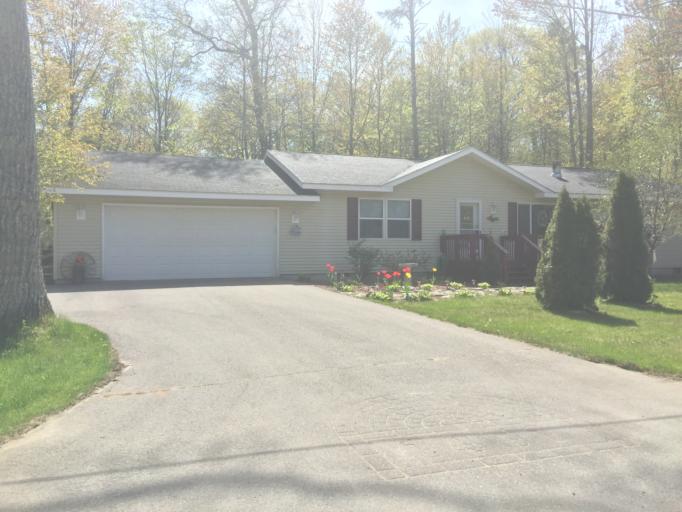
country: US
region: Wisconsin
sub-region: Marinette County
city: Marinette
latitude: 45.1638
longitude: -87.7151
